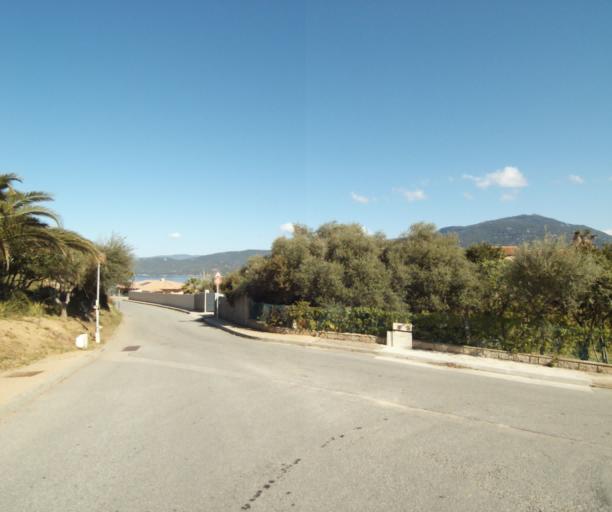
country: FR
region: Corsica
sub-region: Departement de la Corse-du-Sud
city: Propriano
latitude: 41.6693
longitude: 8.8999
